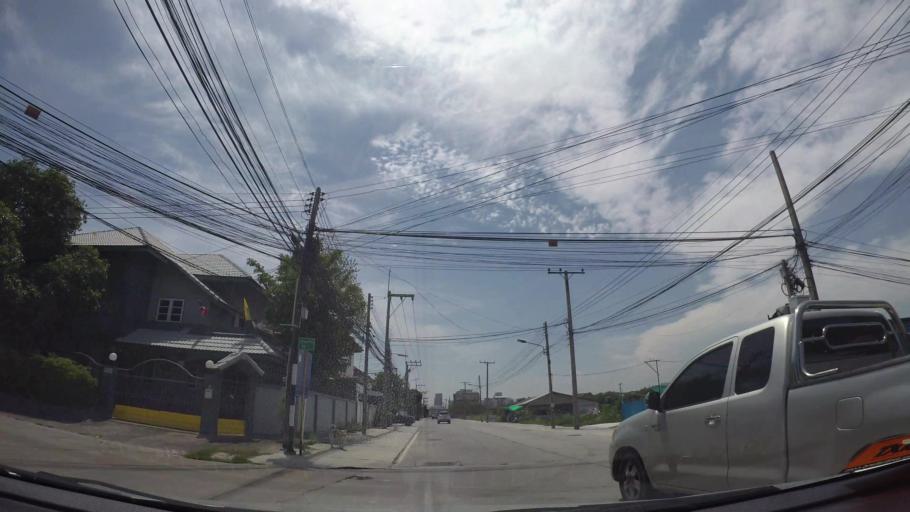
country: TH
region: Chon Buri
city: Chon Buri
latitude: 13.3344
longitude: 100.9483
